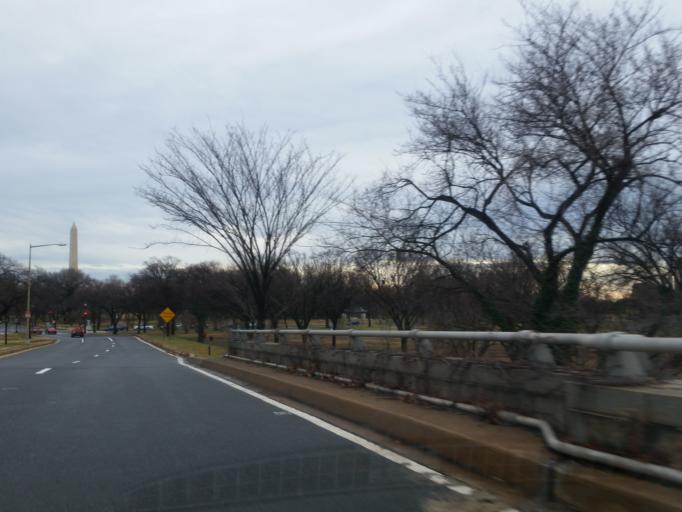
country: US
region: Washington, D.C.
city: Washington, D.C.
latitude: 38.8924
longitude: -77.0525
